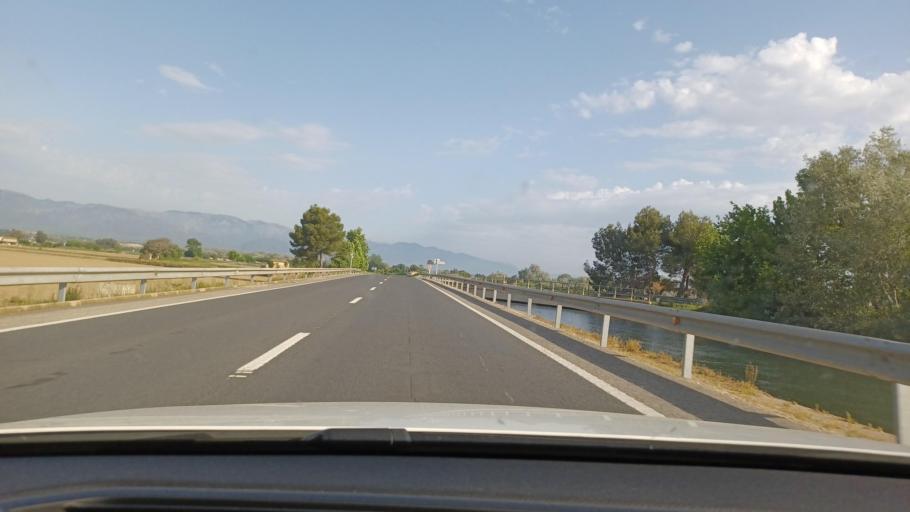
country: ES
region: Catalonia
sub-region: Provincia de Tarragona
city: Tortosa
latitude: 40.7716
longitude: 0.5291
